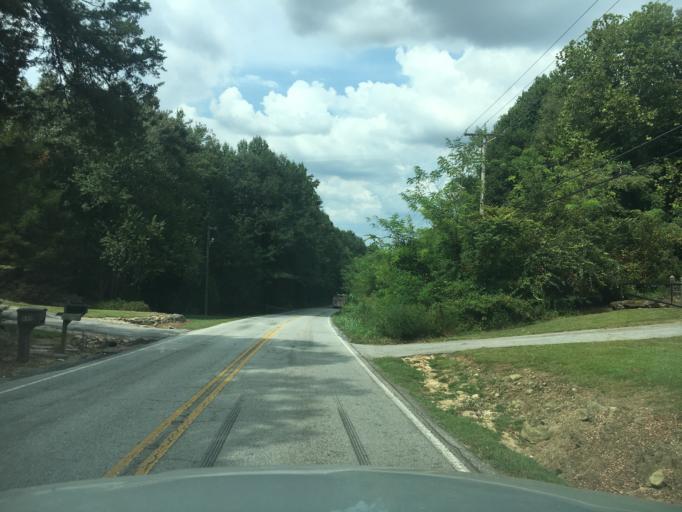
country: US
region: South Carolina
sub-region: Greenville County
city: Five Forks
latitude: 34.8367
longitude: -82.2276
